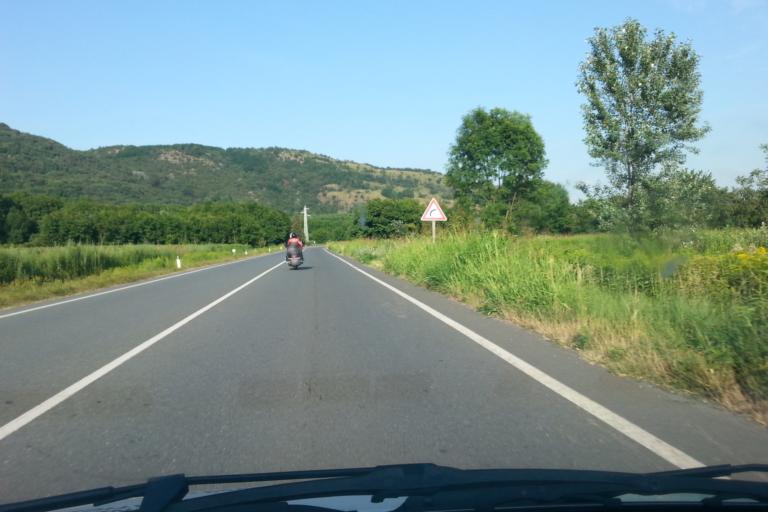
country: IT
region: Piedmont
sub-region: Provincia di Torino
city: Sant'Ambrogio di Torino
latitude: 45.1134
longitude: 7.3541
